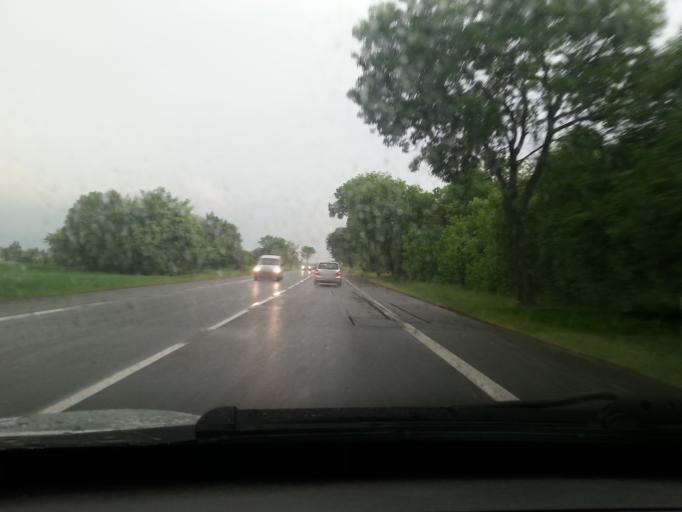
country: PL
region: Lodz Voivodeship
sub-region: Powiat zgierski
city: Strykow
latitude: 51.8536
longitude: 19.5633
